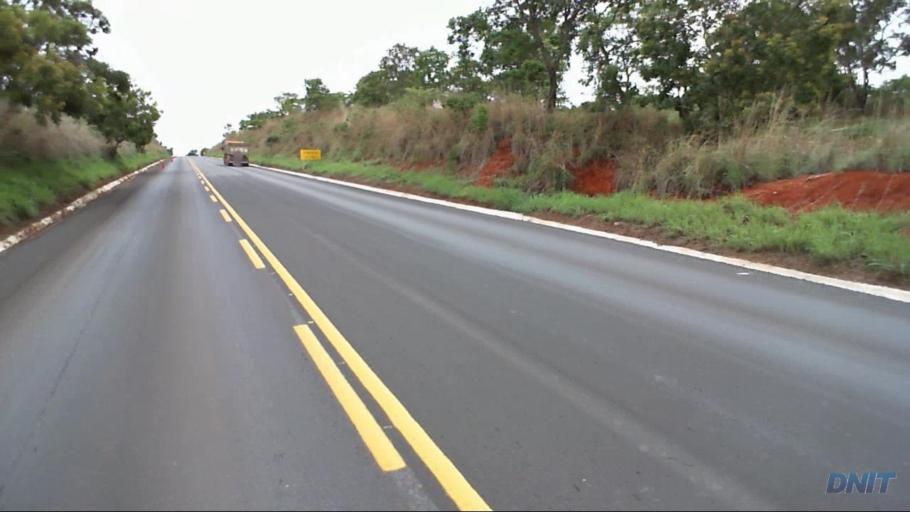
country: BR
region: Goias
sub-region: Padre Bernardo
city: Padre Bernardo
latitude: -15.1788
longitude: -48.4202
